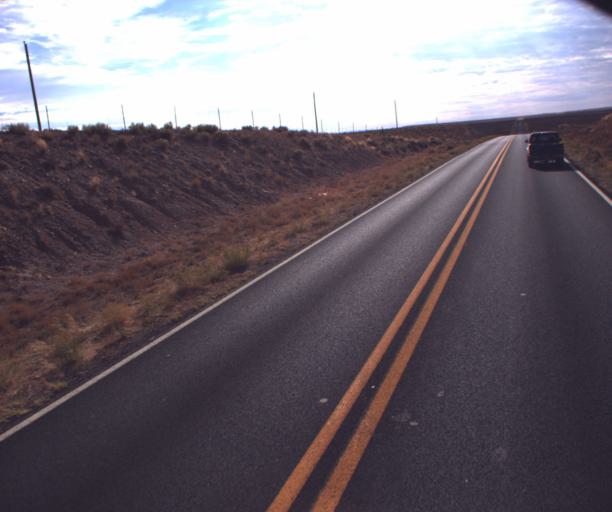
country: US
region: Arizona
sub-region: Apache County
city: Many Farms
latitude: 36.6002
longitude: -109.5691
